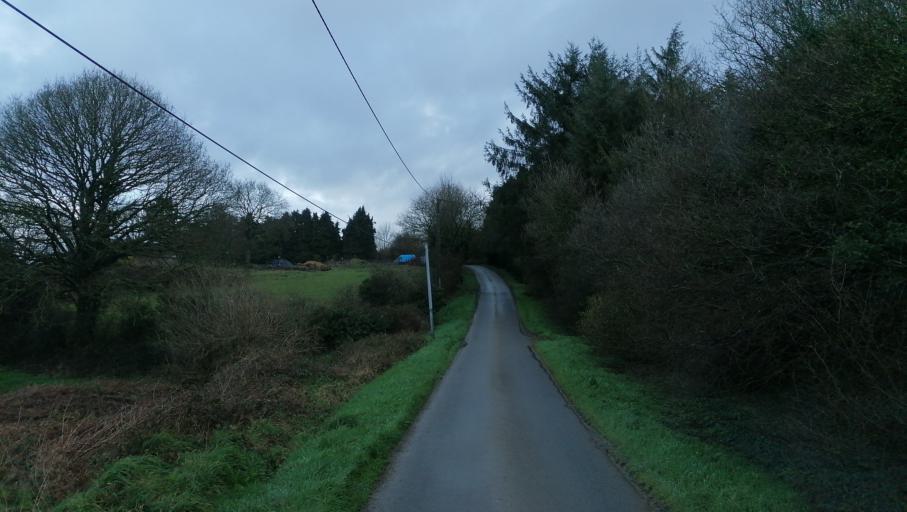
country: FR
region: Brittany
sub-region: Departement des Cotes-d'Armor
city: Lanrodec
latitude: 48.4881
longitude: -3.0037
